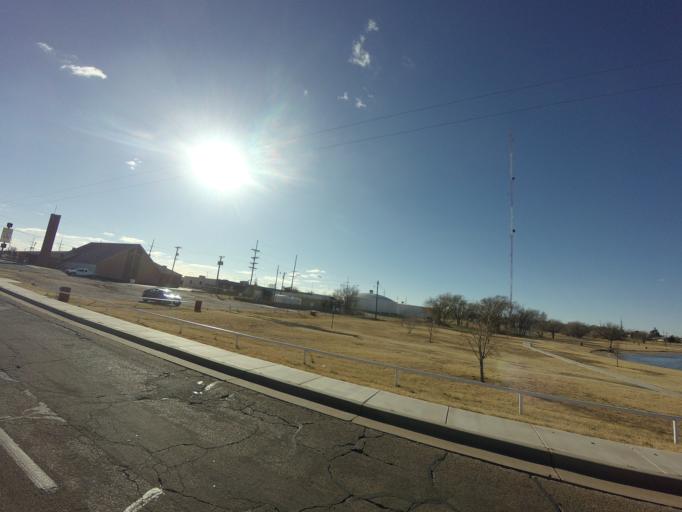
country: US
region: New Mexico
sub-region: Curry County
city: Clovis
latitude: 34.4162
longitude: -103.2054
